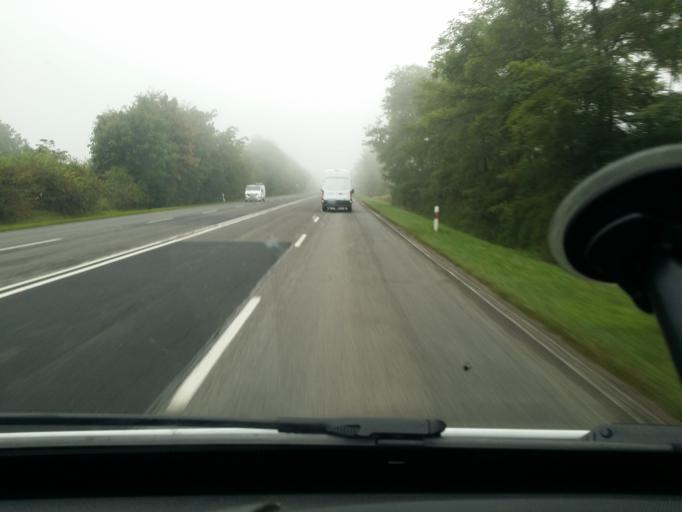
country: HU
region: Bacs-Kiskun
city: Kecskemet
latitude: 46.9547
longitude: 19.6481
